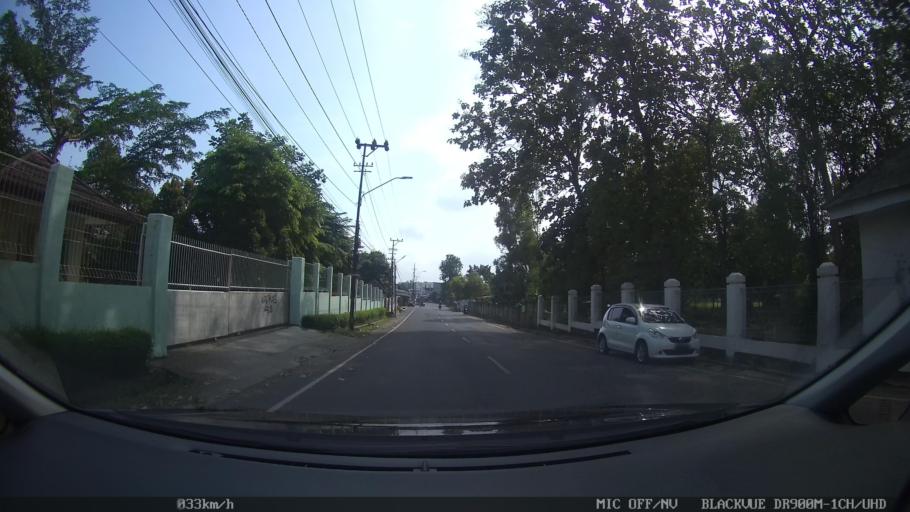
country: ID
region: Lampung
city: Kedaton
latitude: -5.3751
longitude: 105.2507
